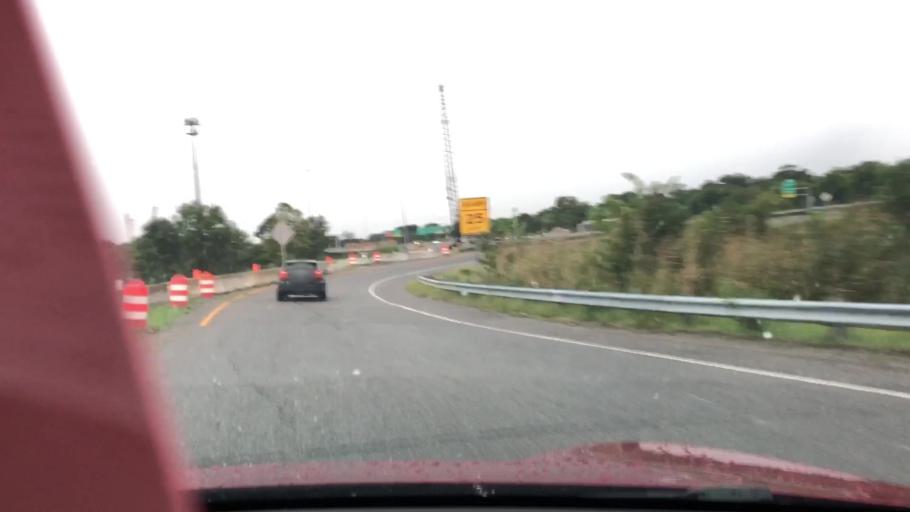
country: US
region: Virginia
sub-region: City of Chesapeake
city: Chesapeake
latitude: 36.8444
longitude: -76.1851
